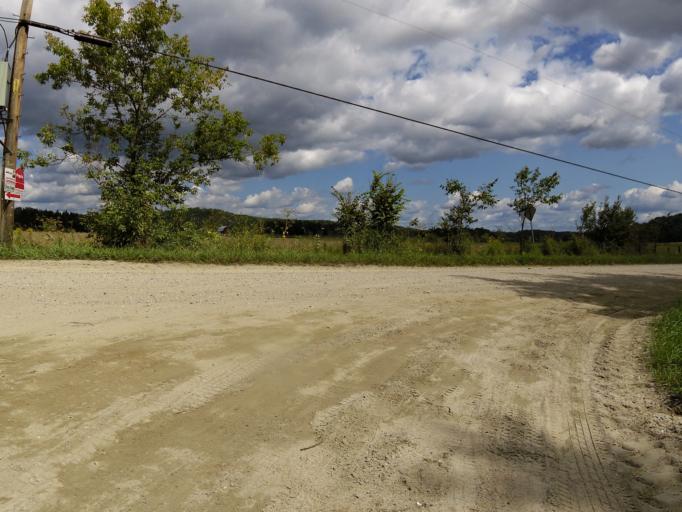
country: CA
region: Quebec
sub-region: Outaouais
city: Wakefield
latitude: 45.7848
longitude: -76.0310
